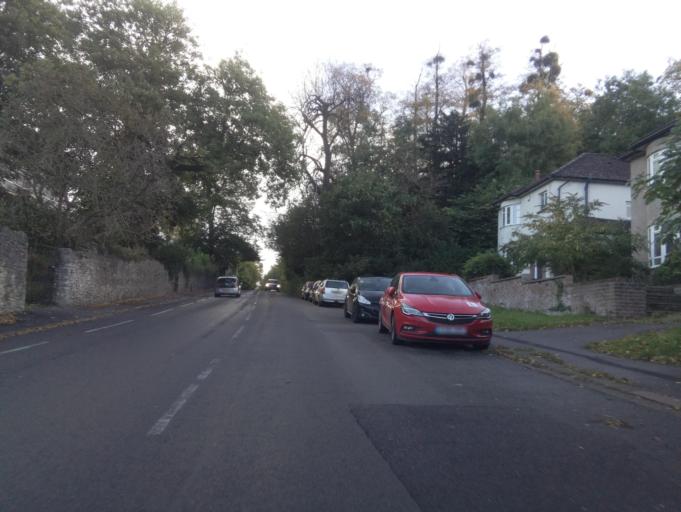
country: GB
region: England
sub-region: Bristol
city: Bristol
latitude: 51.5016
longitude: -2.6251
